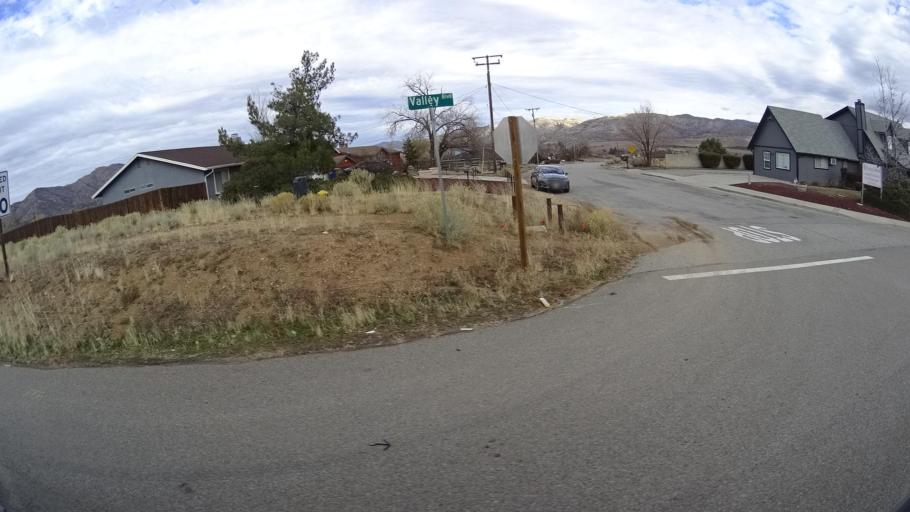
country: US
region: California
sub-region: Kern County
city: Golden Hills
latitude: 35.1243
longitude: -118.4817
